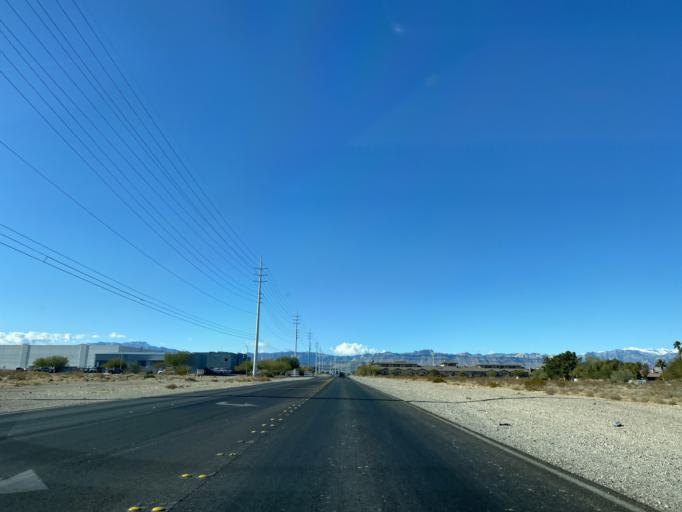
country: US
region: Nevada
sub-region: Clark County
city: Spring Valley
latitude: 36.0714
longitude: -115.2164
